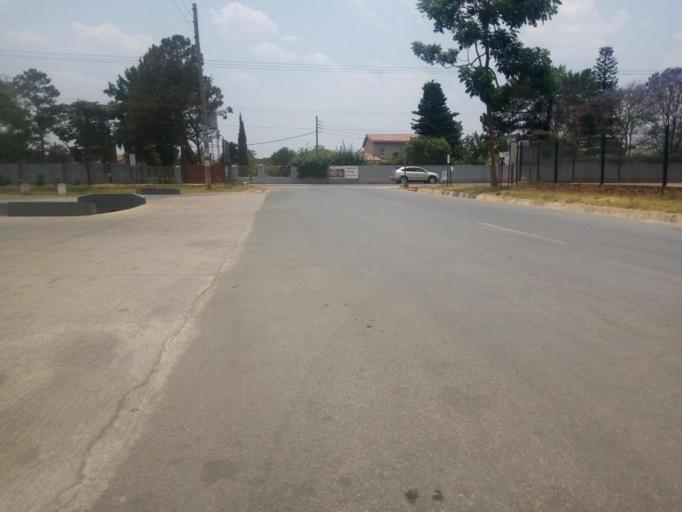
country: ZM
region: Lusaka
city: Lusaka
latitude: -15.3964
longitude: 28.3943
